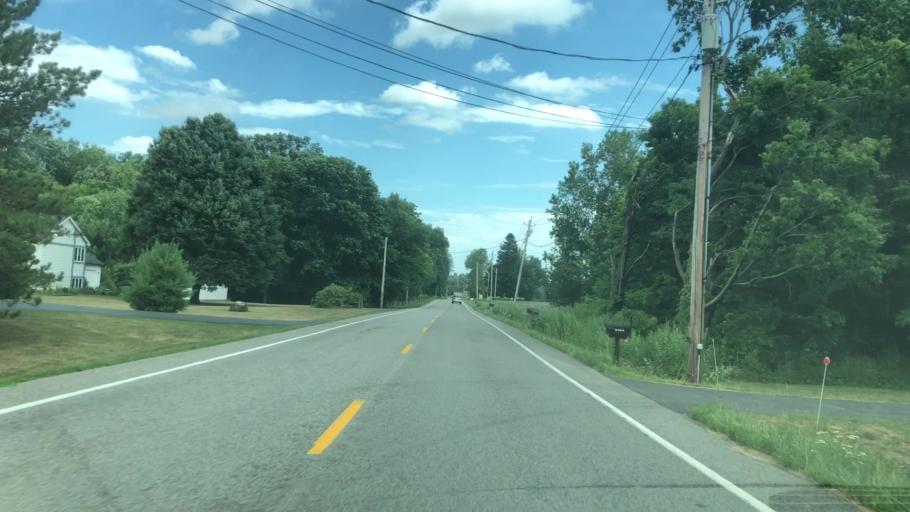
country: US
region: New York
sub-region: Wayne County
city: Macedon
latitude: 43.1134
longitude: -77.3524
